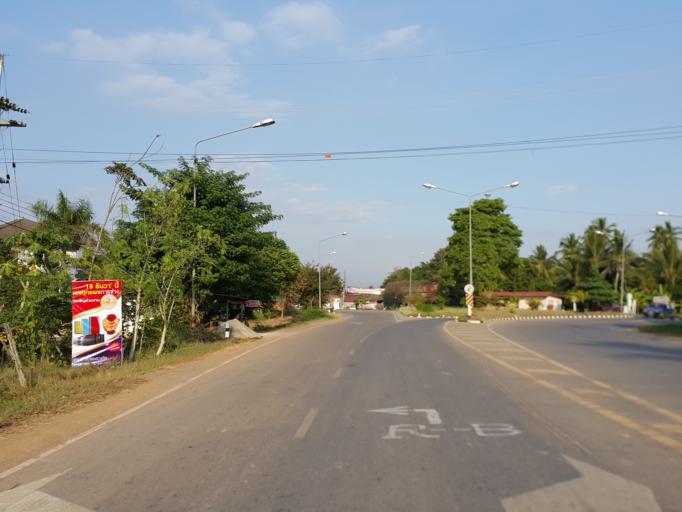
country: TH
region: Sukhothai
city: Sawankhalok
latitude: 17.3965
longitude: 99.7953
